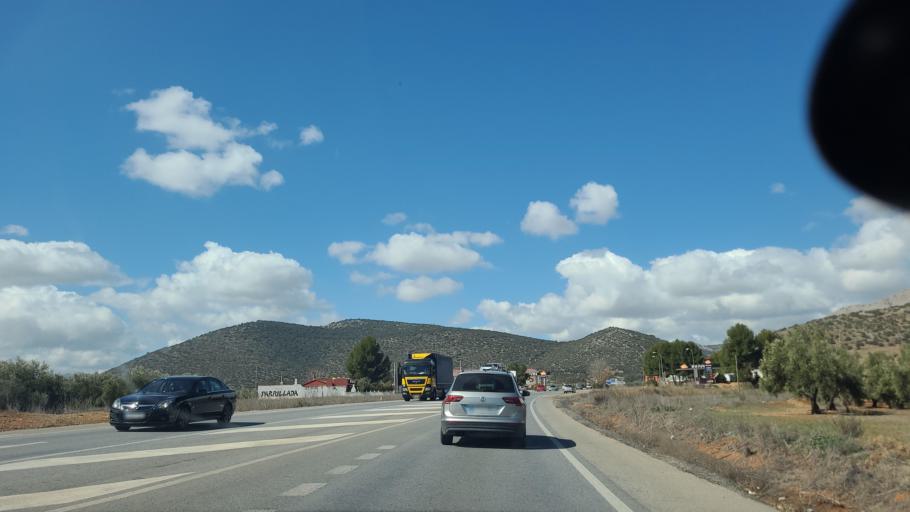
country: ES
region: Andalusia
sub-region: Provincia de Granada
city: Iznalloz
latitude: 37.4005
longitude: -3.5519
